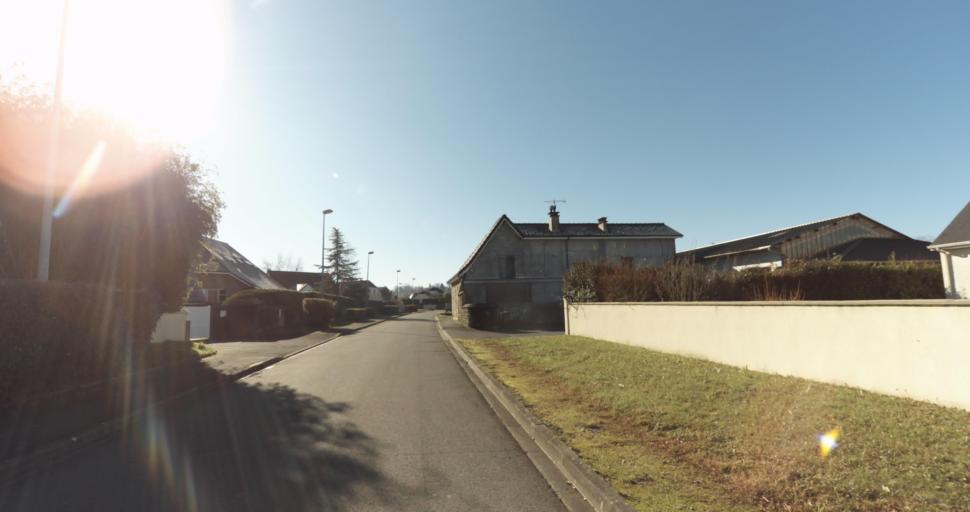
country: FR
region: Aquitaine
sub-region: Departement des Pyrenees-Atlantiques
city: Morlaas
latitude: 43.3509
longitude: -0.2659
